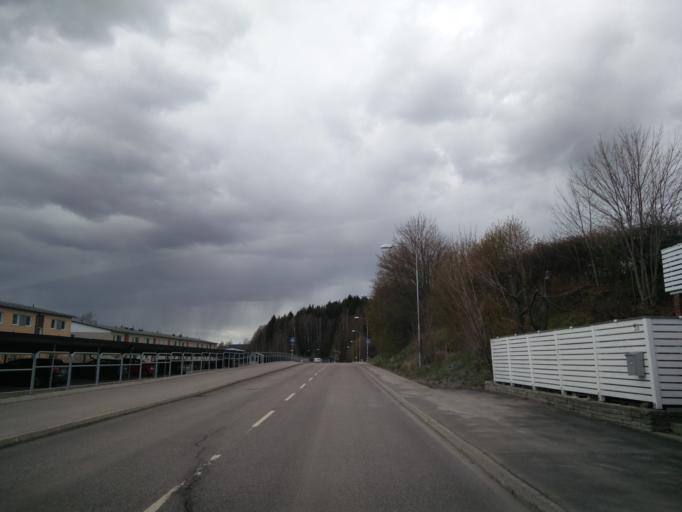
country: SE
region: Vaesternorrland
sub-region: Sundsvalls Kommun
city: Sundsvall
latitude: 62.4055
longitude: 17.2580
